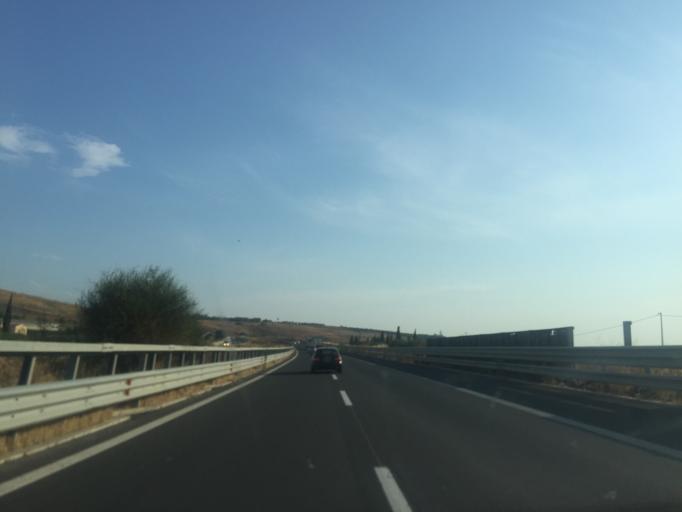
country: IT
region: Sicily
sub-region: Provincia di Siracusa
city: Carlentini
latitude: 37.3528
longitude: 15.0464
